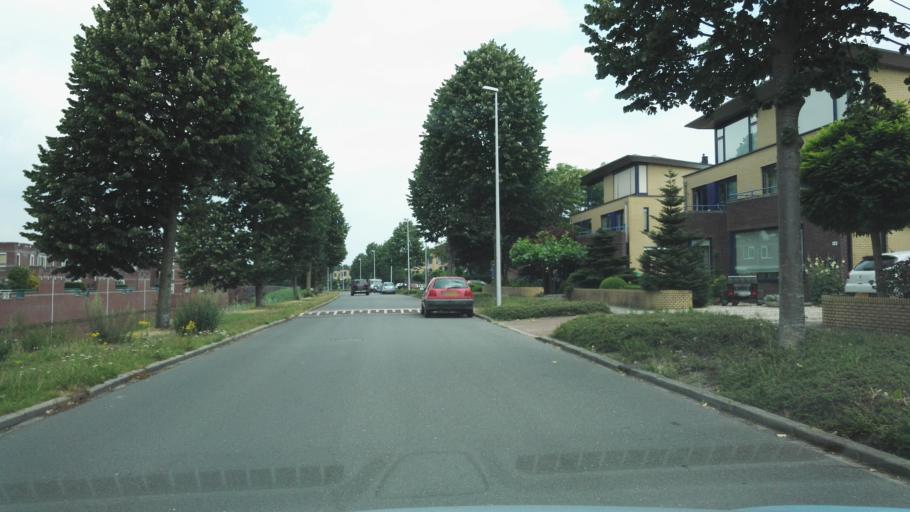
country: NL
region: Gelderland
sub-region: Gemeente Apeldoorn
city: Apeldoorn
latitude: 52.2114
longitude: 6.0144
